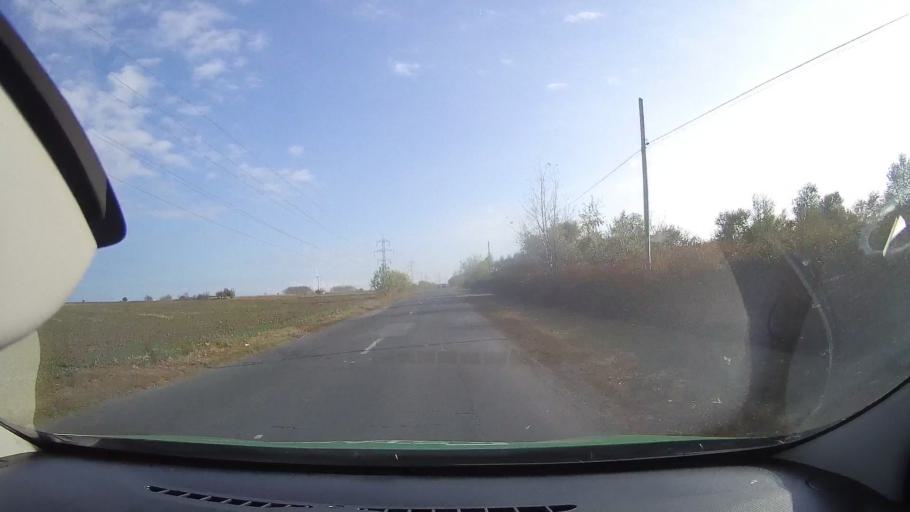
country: RO
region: Constanta
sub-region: Comuna Corbu
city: Corbu
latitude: 44.3727
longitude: 28.6656
